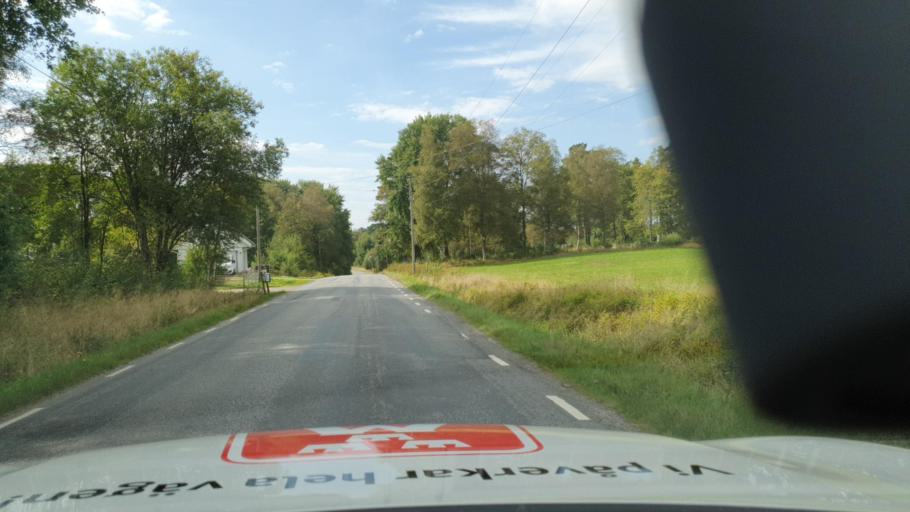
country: SE
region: Vaestra Goetaland
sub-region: Marks Kommun
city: Kinna
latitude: 57.3946
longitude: 12.7926
